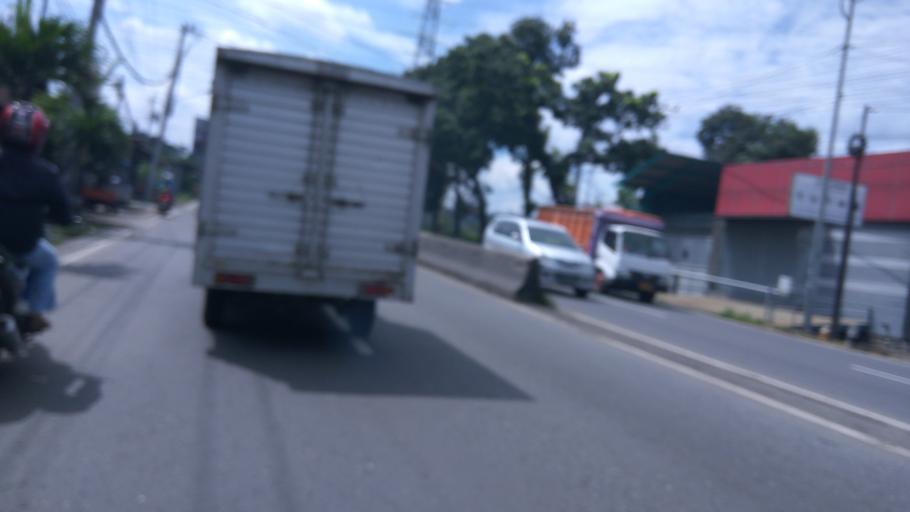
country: ID
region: Central Java
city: Ungaran
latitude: -7.1551
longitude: 110.4106
